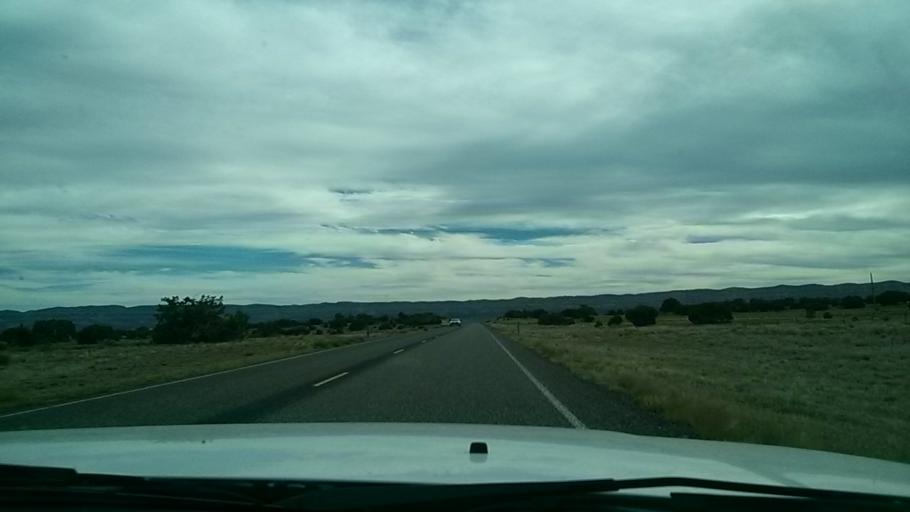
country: US
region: Utah
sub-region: Wayne County
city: Loa
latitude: 37.7411
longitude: -111.5039
